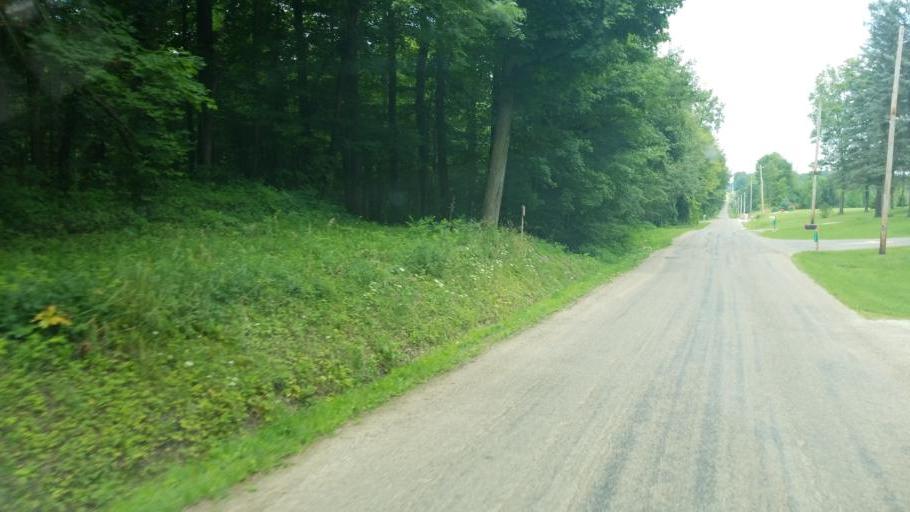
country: US
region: Ohio
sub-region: Richland County
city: Lexington
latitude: 40.6870
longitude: -82.6457
